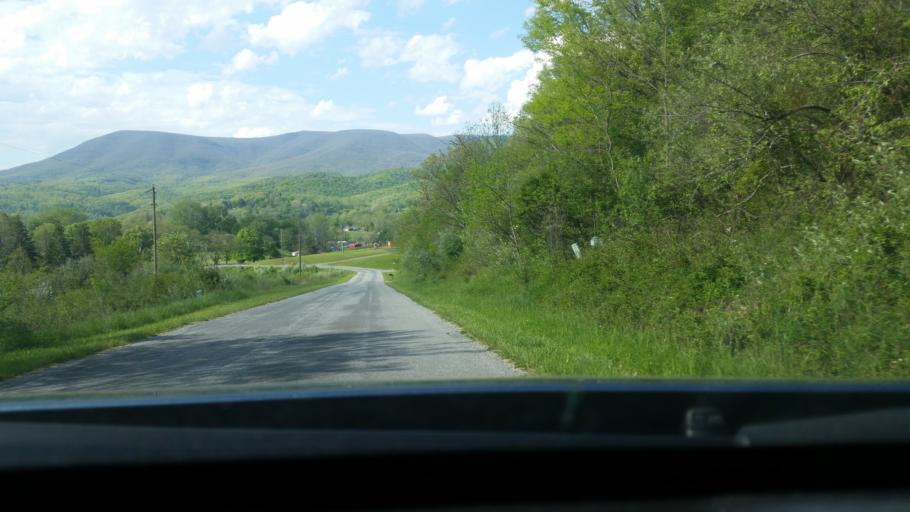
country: US
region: Virginia
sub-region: Giles County
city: Pembroke
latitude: 37.3088
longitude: -80.6327
